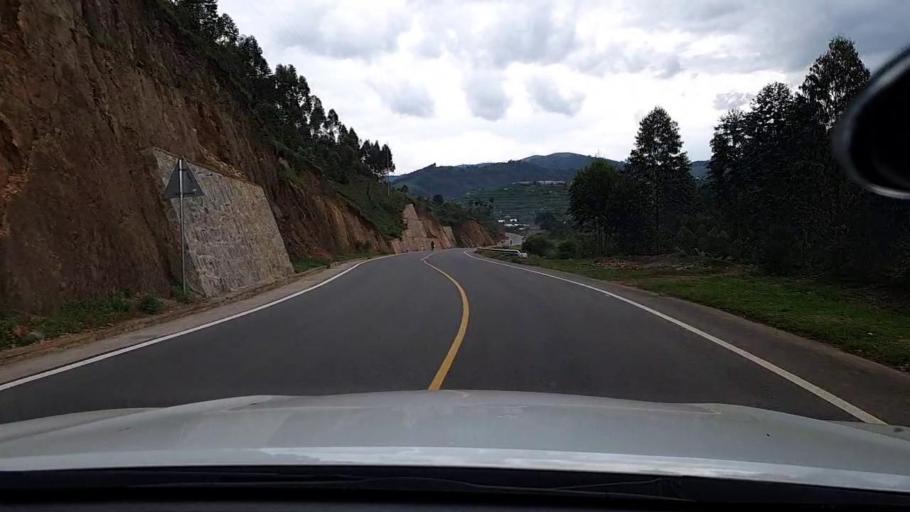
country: RW
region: Northern Province
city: Byumba
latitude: -1.6415
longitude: 29.9258
